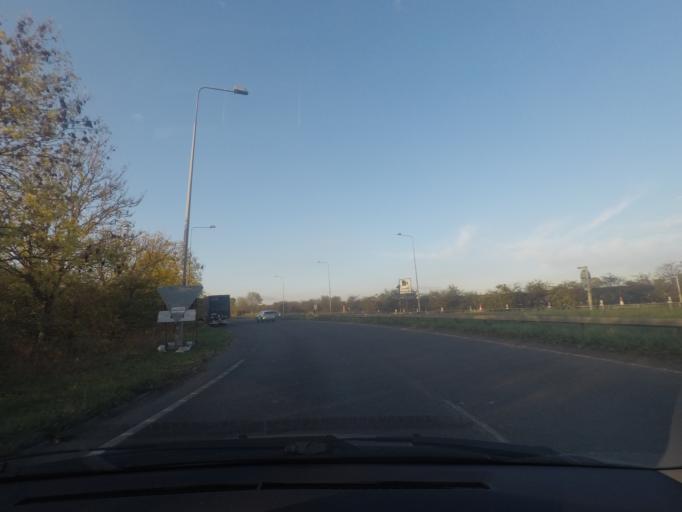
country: GB
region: England
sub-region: North Lincolnshire
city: Barnetby le Wold
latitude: 53.5867
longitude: -0.4145
